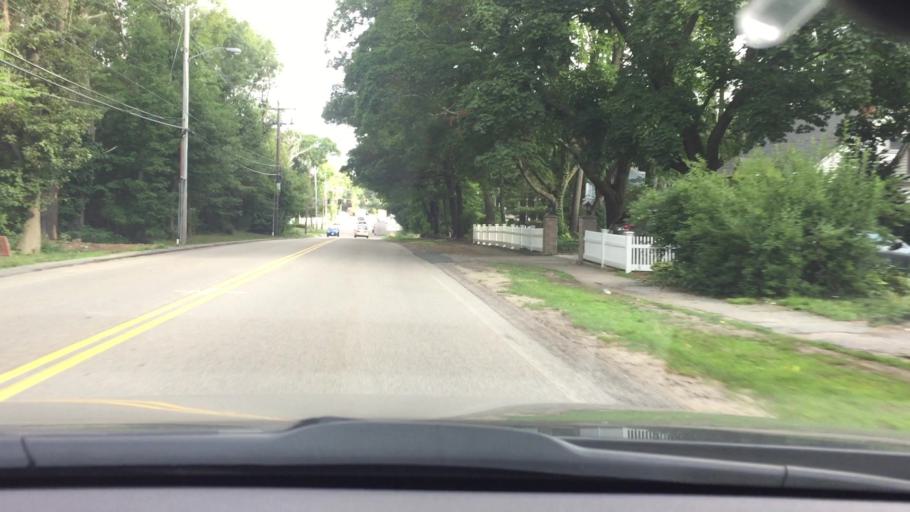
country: US
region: Massachusetts
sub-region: Norfolk County
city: Sharon
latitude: 42.1515
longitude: -71.2026
